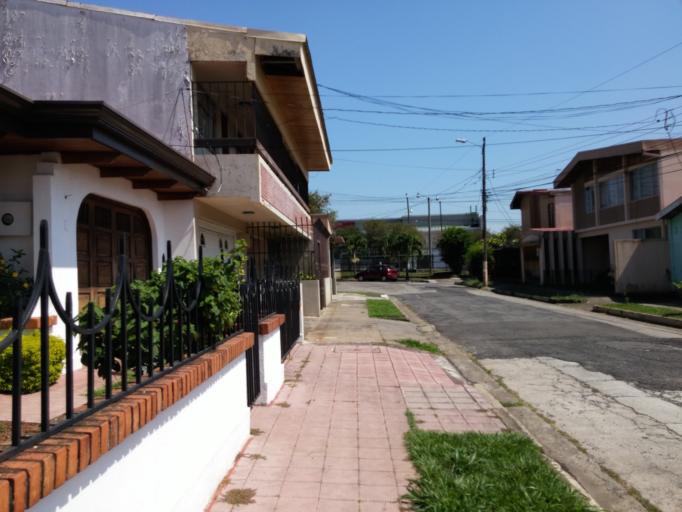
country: CR
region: Alajuela
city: Alajuela
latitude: 10.0124
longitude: -84.2087
